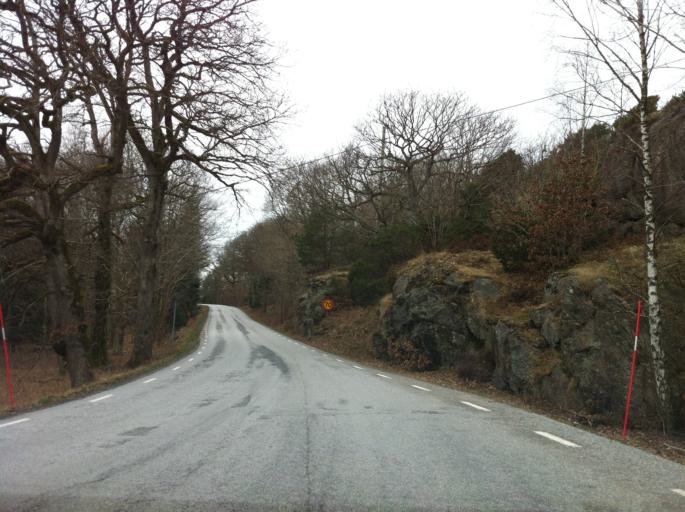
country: SE
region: Vaestra Goetaland
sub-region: Orust
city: Henan
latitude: 58.2700
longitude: 11.6926
